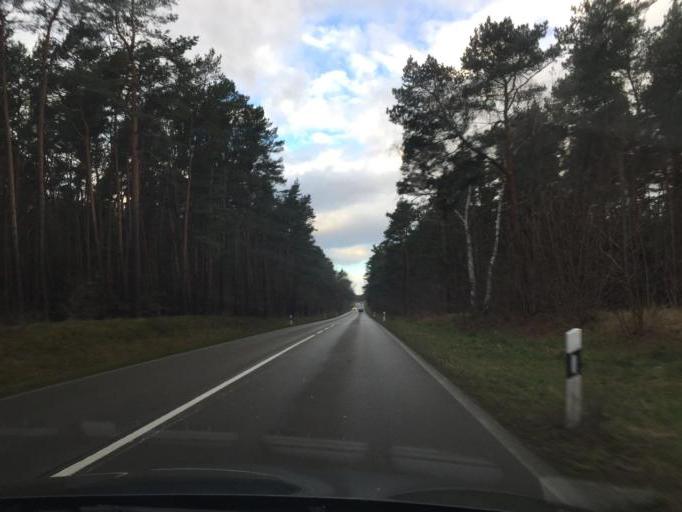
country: DE
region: Brandenburg
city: Kolkwitz
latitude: 51.7513
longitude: 14.2005
